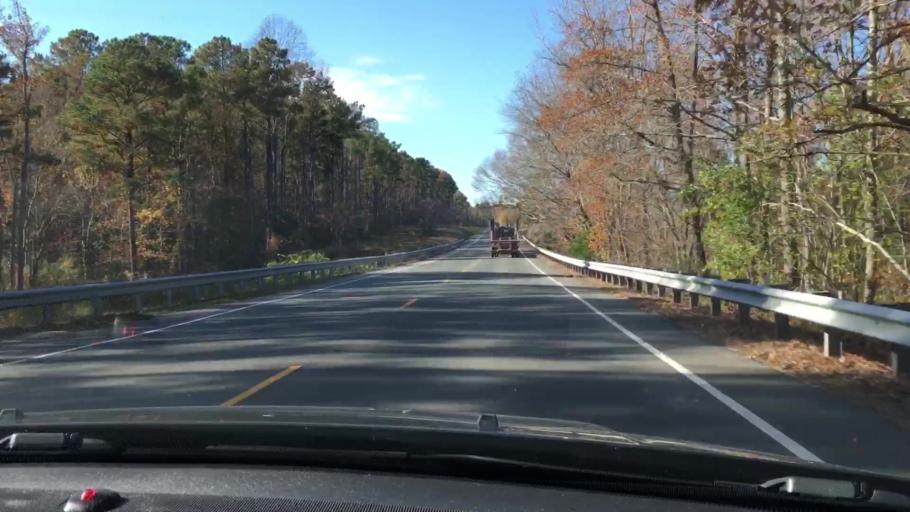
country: US
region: Virginia
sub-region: King William County
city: Central Garage
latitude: 37.7869
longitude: -77.1761
